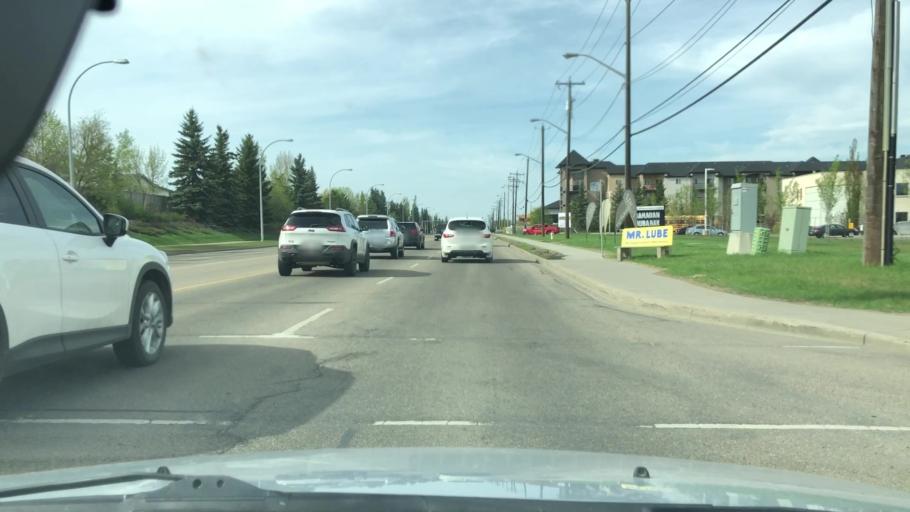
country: CA
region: Alberta
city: Edmonton
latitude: 53.6067
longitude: -113.5412
